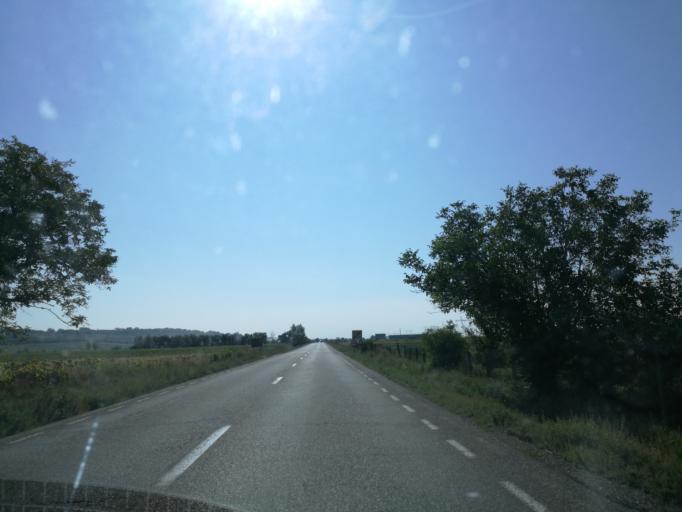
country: RO
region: Suceava
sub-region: Comuna Forasti
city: Oniceni
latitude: 47.3400
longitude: 26.4314
